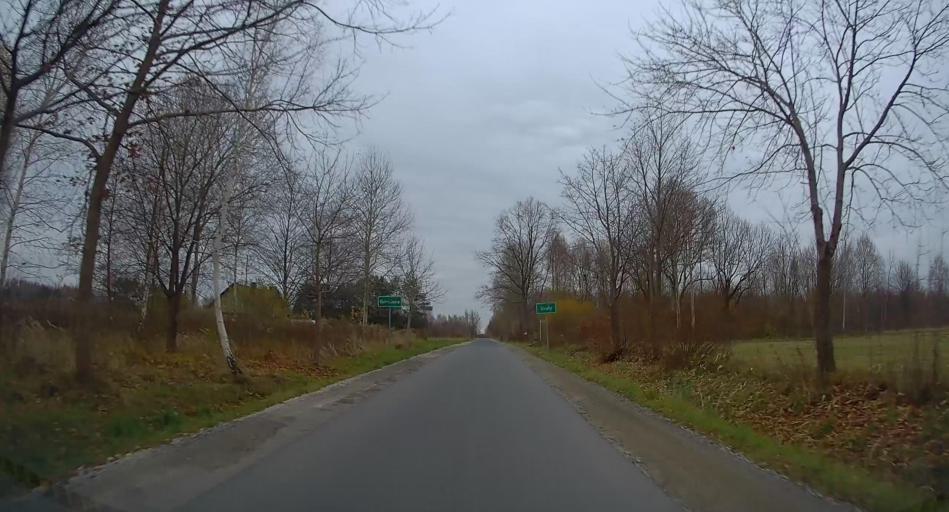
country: PL
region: Lodz Voivodeship
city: Zabia Wola
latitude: 51.9975
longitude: 20.6588
